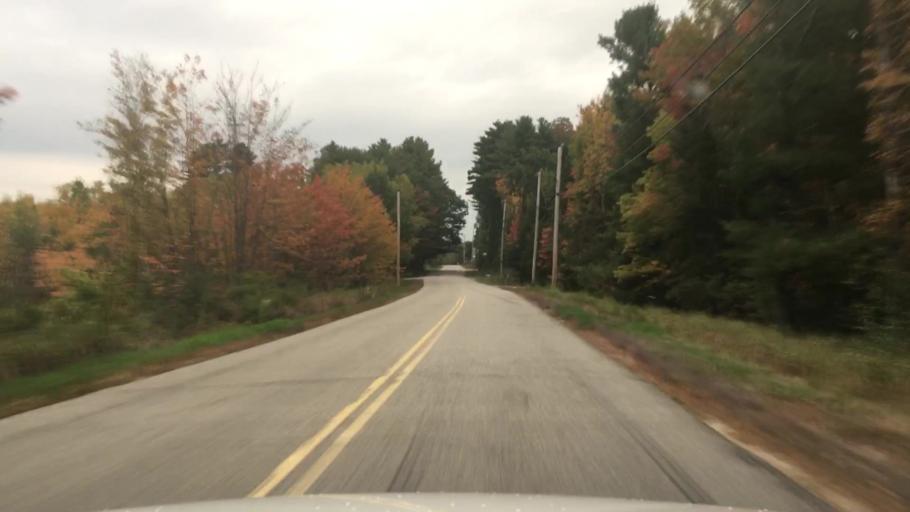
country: US
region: Maine
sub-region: York County
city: Buxton
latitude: 43.6430
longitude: -70.5257
